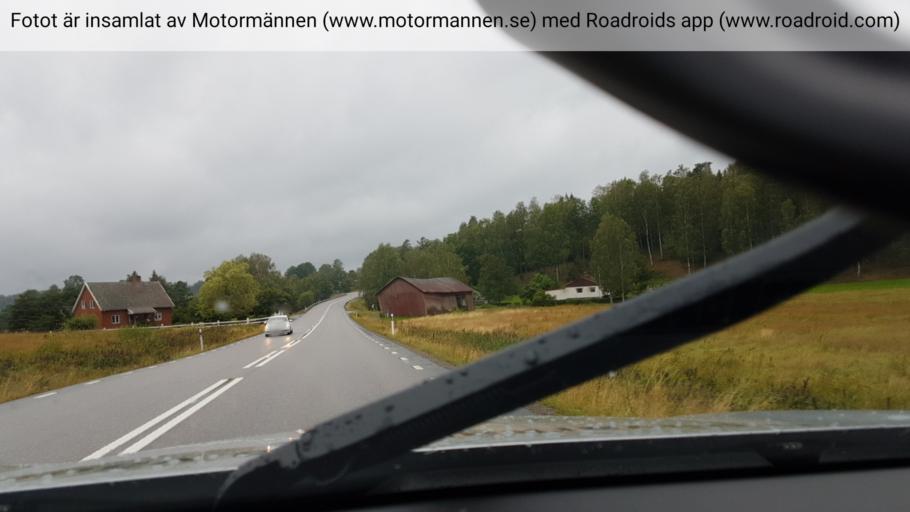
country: SE
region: Vaestra Goetaland
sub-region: Bengtsfors Kommun
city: Billingsfors
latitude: 59.0310
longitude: 12.3074
